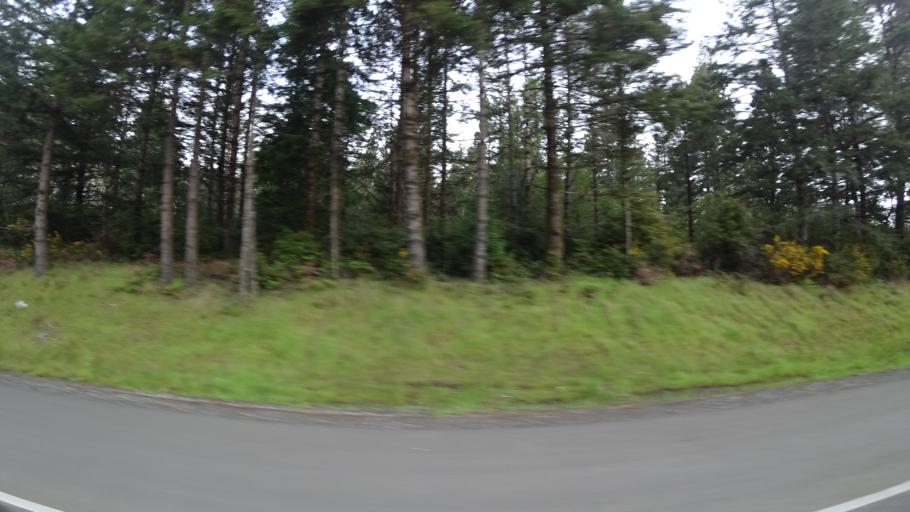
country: US
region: Oregon
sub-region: Coos County
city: Bandon
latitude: 43.1811
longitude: -124.3630
